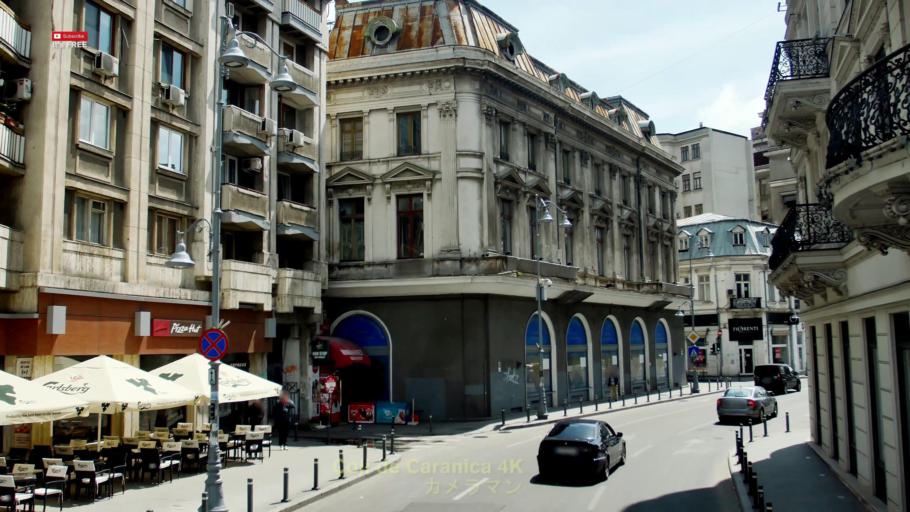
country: RO
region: Bucuresti
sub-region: Municipiul Bucuresti
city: Bucuresti
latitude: 44.4339
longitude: 26.0979
